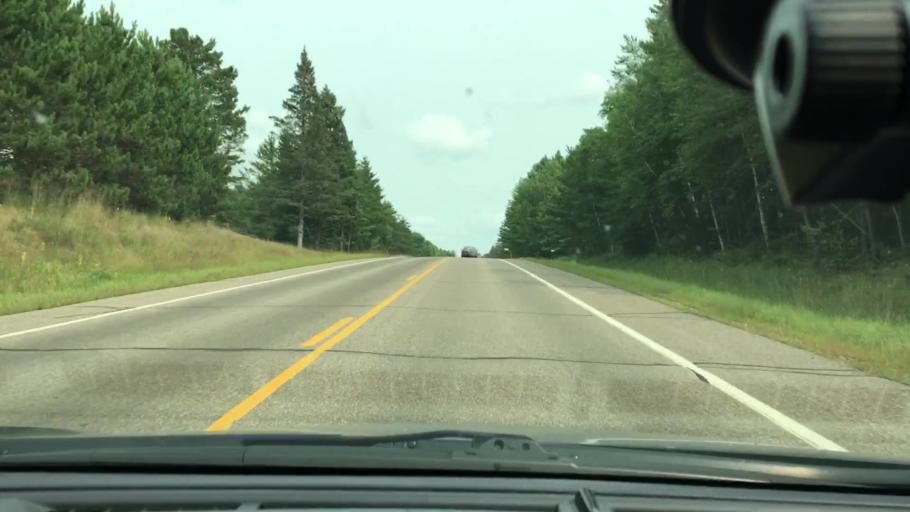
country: US
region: Minnesota
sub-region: Crow Wing County
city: Cross Lake
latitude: 46.7309
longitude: -93.9809
